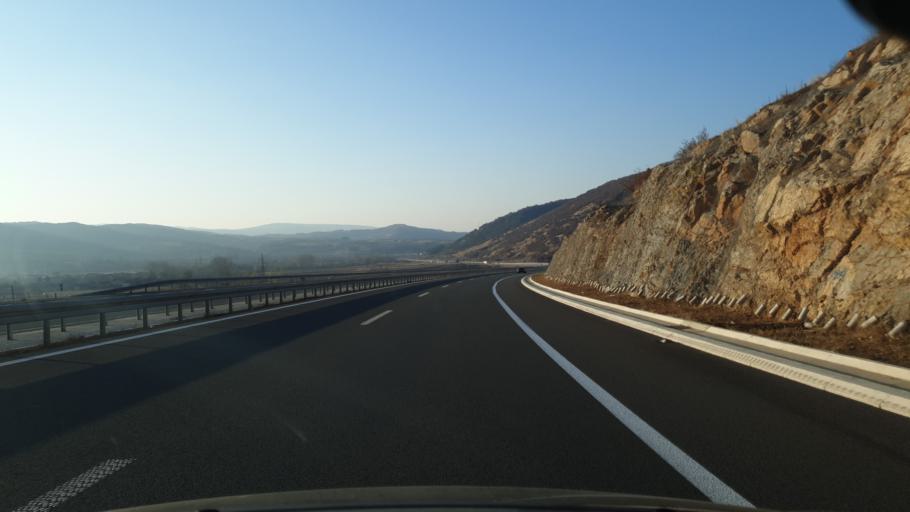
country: RS
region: Central Serbia
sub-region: Pirotski Okrug
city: Dimitrovgrad
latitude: 43.0159
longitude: 22.7521
